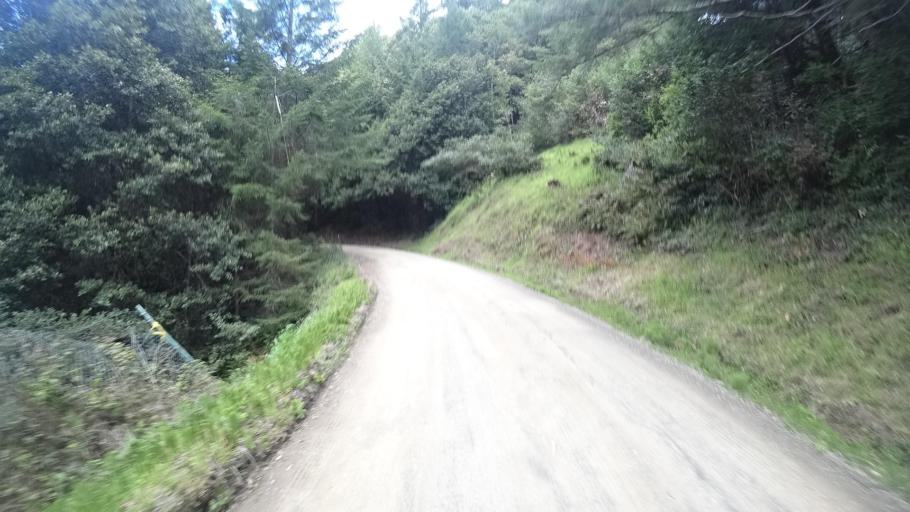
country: US
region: California
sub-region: Humboldt County
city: Blue Lake
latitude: 40.7648
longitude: -123.9546
